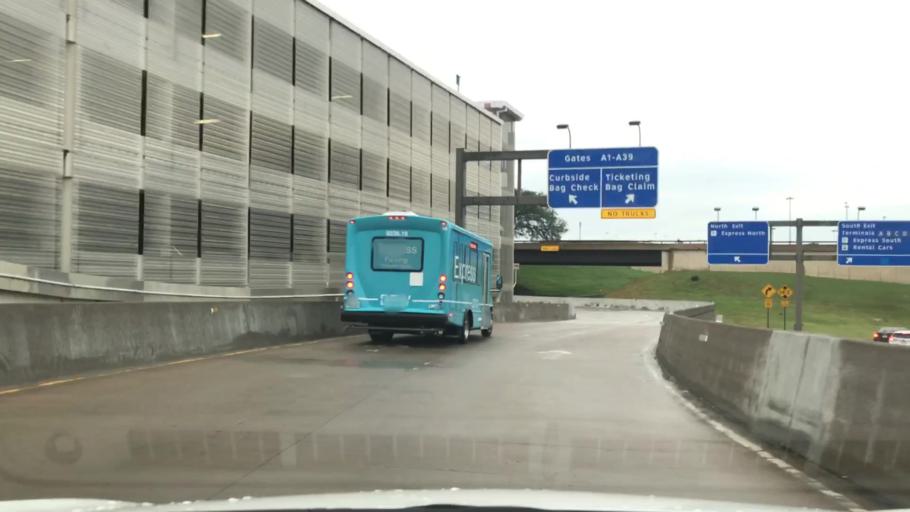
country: US
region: Texas
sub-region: Tarrant County
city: Grapevine
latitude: 32.9038
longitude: -97.0382
